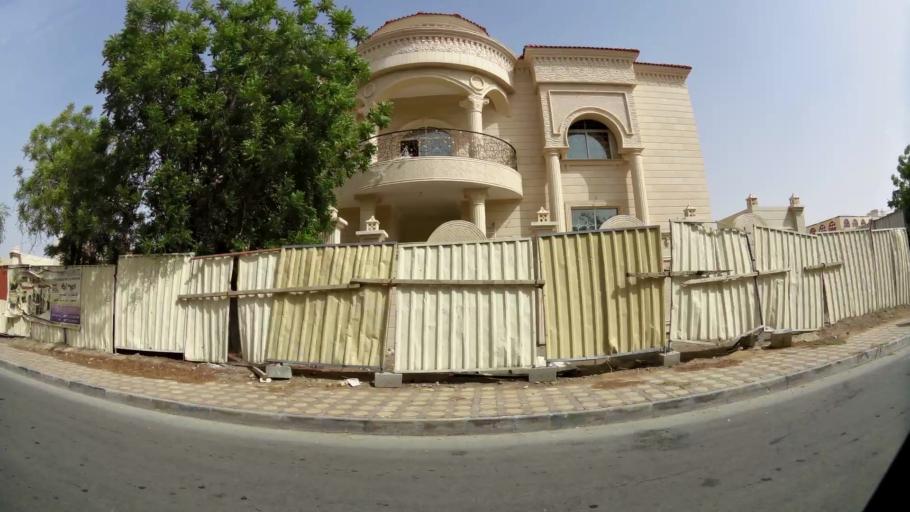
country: AE
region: Abu Dhabi
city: Al Ain
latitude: 24.1911
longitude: 55.6351
